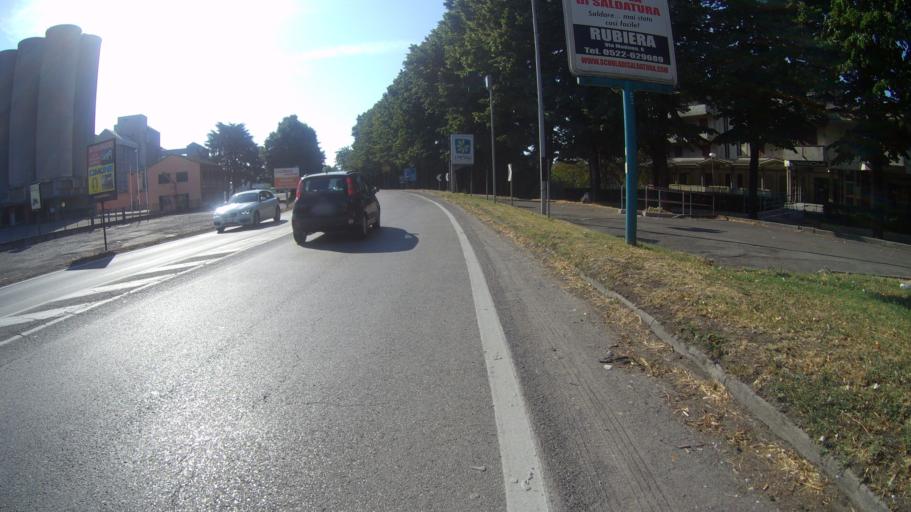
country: IT
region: Emilia-Romagna
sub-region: Provincia di Reggio Emilia
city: Rubiera
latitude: 44.6522
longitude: 10.7880
